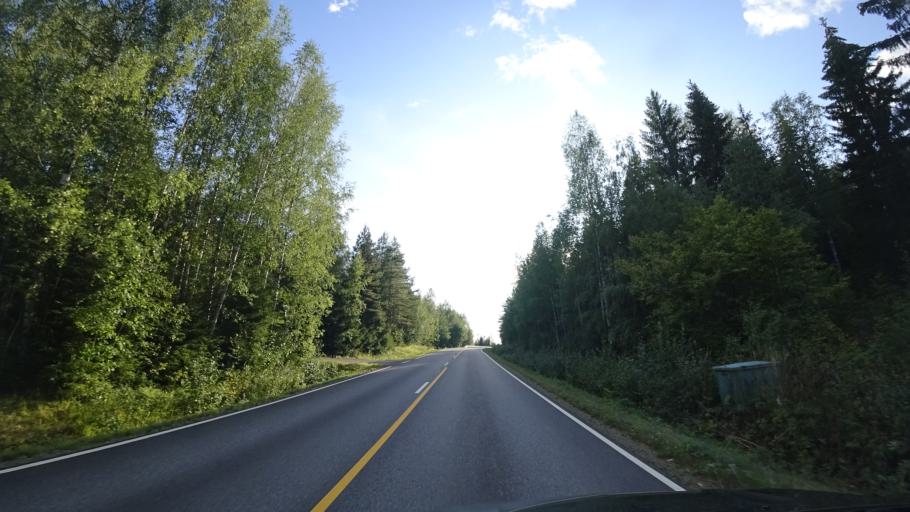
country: FI
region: Haeme
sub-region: Haemeenlinna
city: Lammi
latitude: 61.0759
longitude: 25.0941
